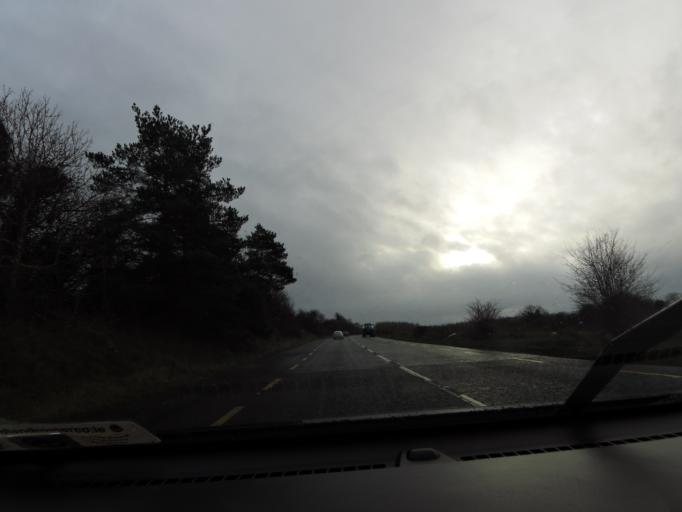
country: IE
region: Munster
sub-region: North Tipperary
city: Roscrea
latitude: 52.9917
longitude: -7.8629
